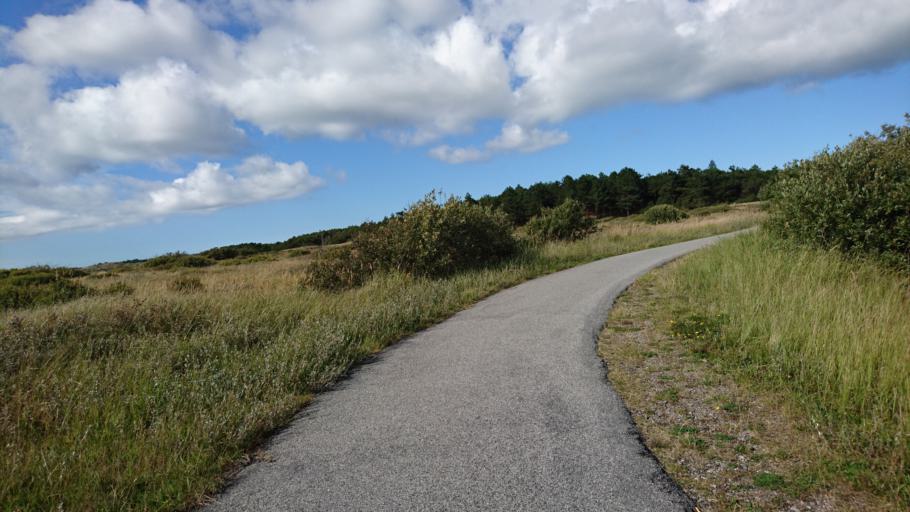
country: DK
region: North Denmark
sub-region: Frederikshavn Kommune
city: Skagen
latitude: 57.6923
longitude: 10.5041
